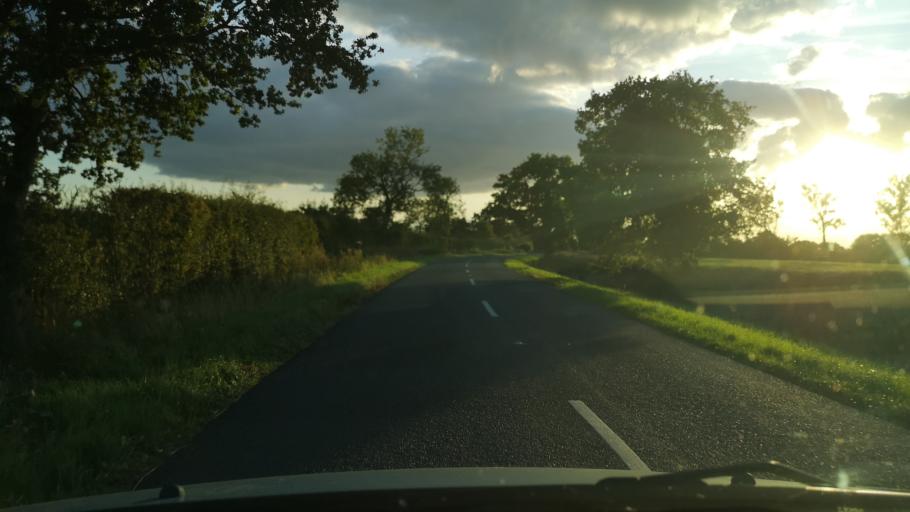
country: GB
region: England
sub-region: Doncaster
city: Fenwick
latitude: 53.6279
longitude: -1.0697
